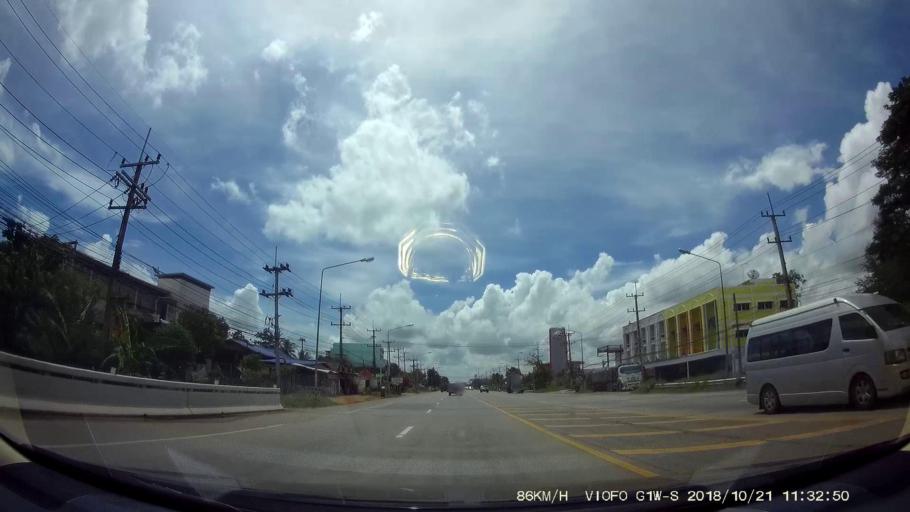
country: TH
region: Chaiyaphum
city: Chaiyaphum
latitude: 15.7531
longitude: 102.0240
